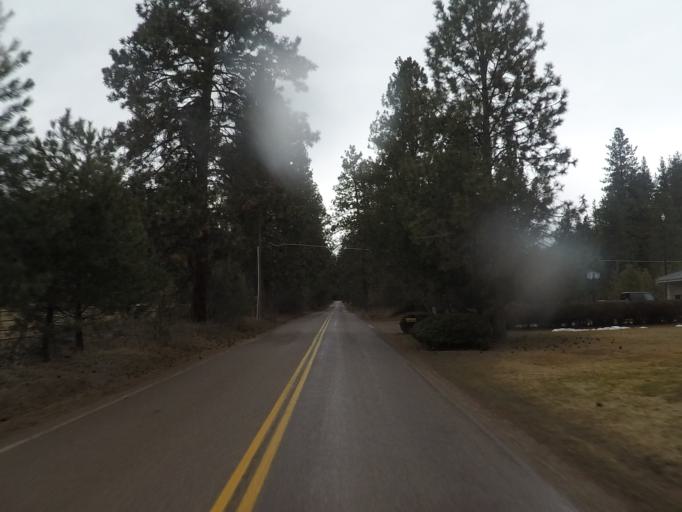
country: US
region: Montana
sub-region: Missoula County
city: East Missoula
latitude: 46.9137
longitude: -113.9603
